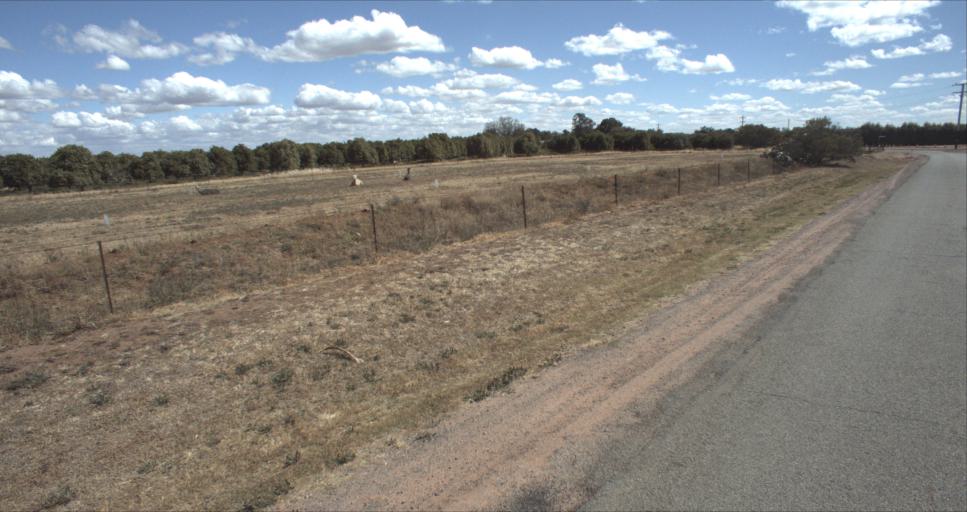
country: AU
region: New South Wales
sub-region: Leeton
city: Leeton
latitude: -34.5127
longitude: 146.2431
